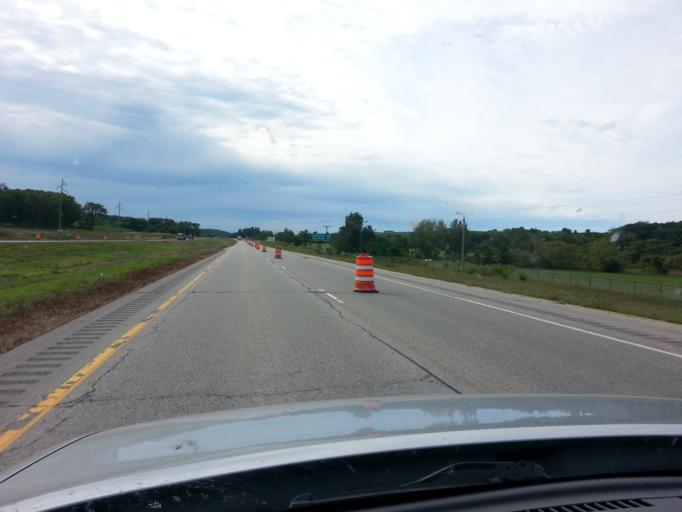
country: US
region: Minnesota
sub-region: Goodhue County
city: Cannon Falls
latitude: 44.4730
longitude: -92.9082
